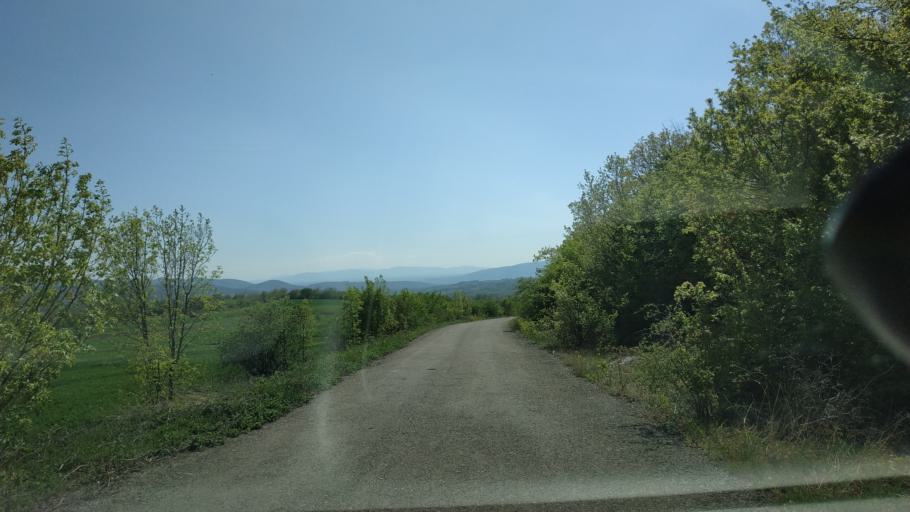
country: RS
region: Central Serbia
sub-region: Zajecarski Okrug
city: Soko Banja
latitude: 43.4986
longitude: 21.8830
